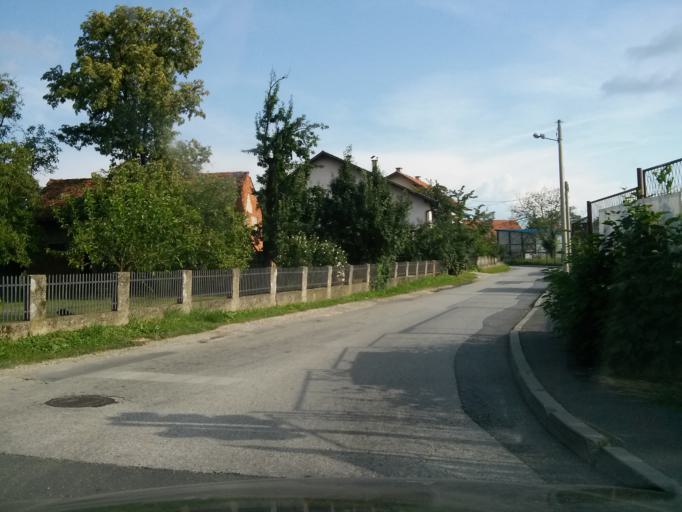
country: HR
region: Grad Zagreb
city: Zadvorsko
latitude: 45.7679
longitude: 15.9352
